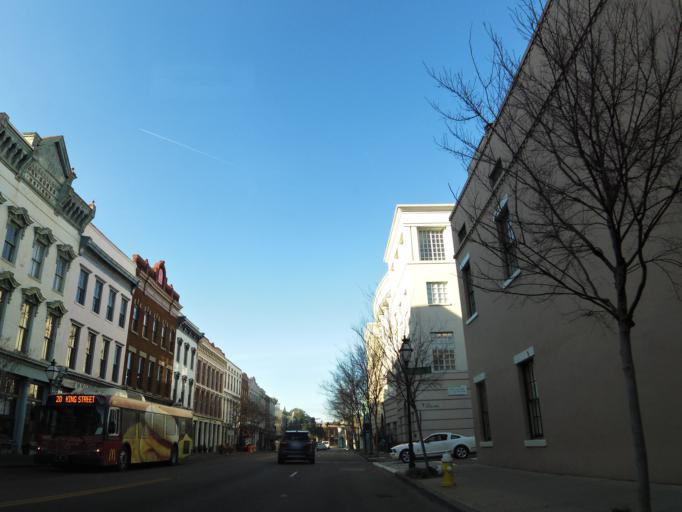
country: US
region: South Carolina
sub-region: Charleston County
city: Charleston
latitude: 32.7813
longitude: -79.9317
